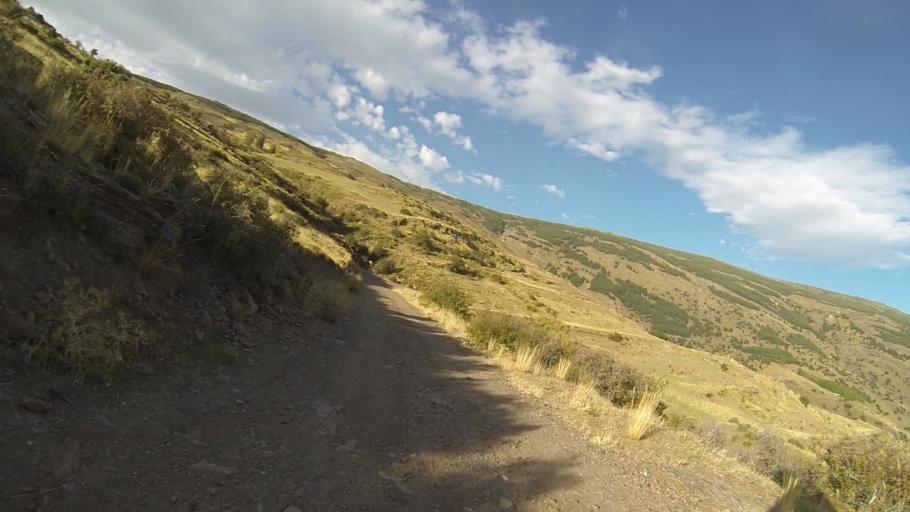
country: ES
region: Andalusia
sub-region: Provincia de Almeria
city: Laujar de Andarax
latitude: 37.0666
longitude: -2.8849
